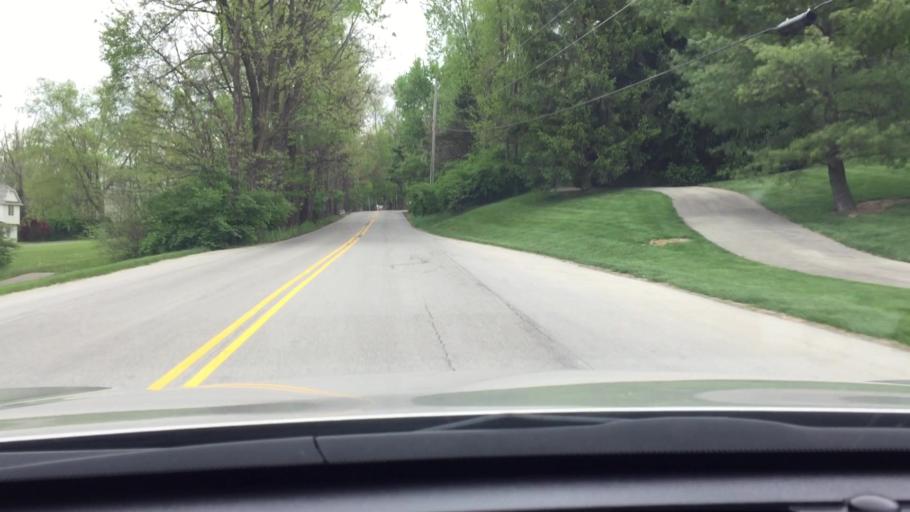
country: US
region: Indiana
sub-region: Hamilton County
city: Carmel
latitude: 39.9954
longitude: -86.0612
